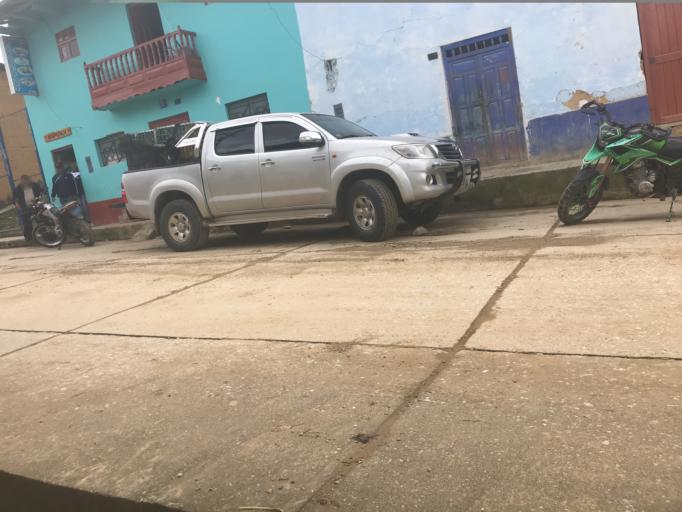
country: PE
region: Cajamarca
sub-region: Provincia de Chota
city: Querocoto
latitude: -6.3614
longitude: -79.0331
